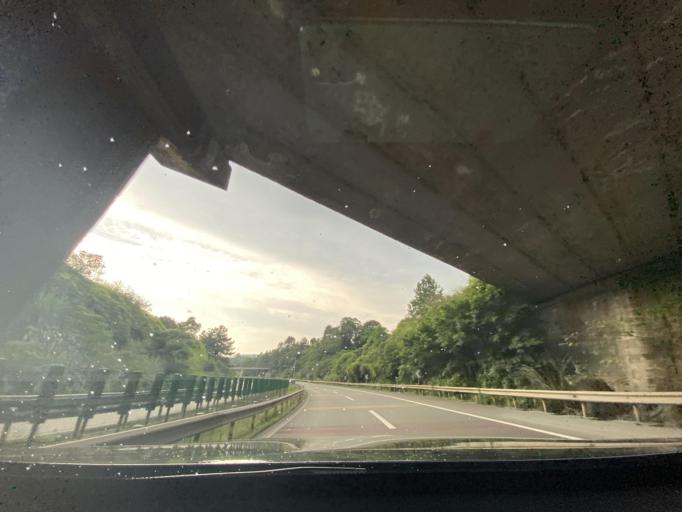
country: CN
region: Sichuan
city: Chonglong
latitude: 29.8059
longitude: 104.7096
